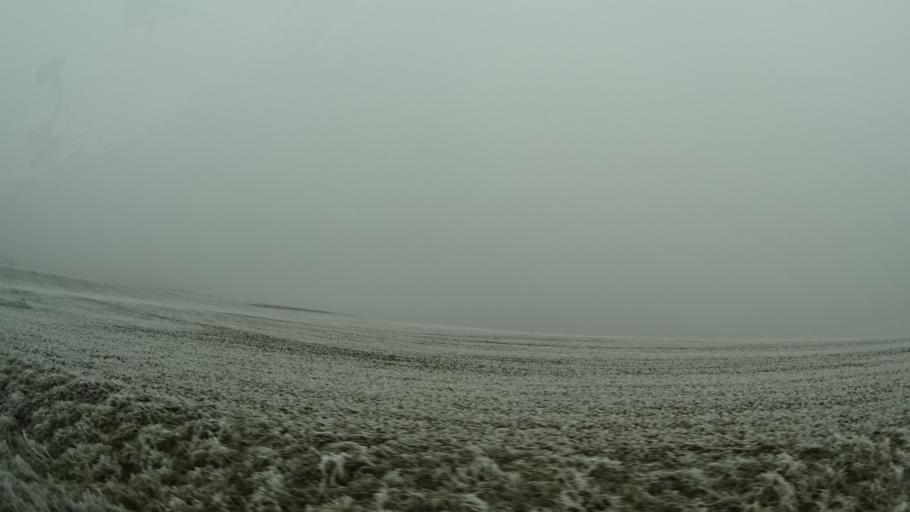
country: DE
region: Bavaria
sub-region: Regierungsbezirk Unterfranken
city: Willmars
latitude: 50.5222
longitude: 10.2996
